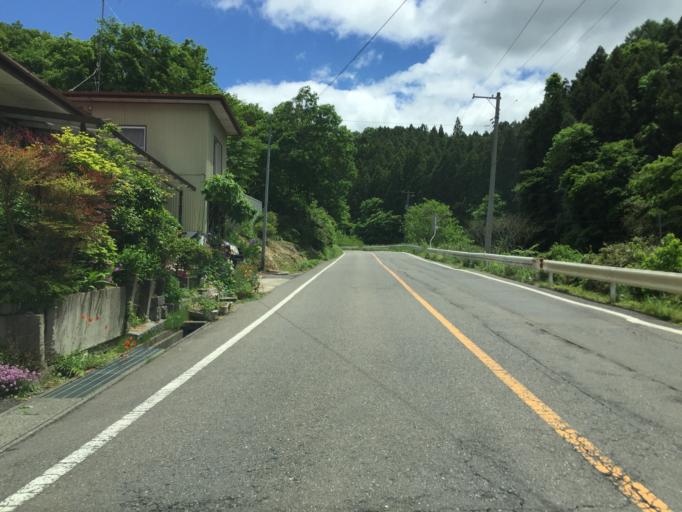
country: JP
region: Fukushima
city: Motomiya
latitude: 37.5190
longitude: 140.4526
